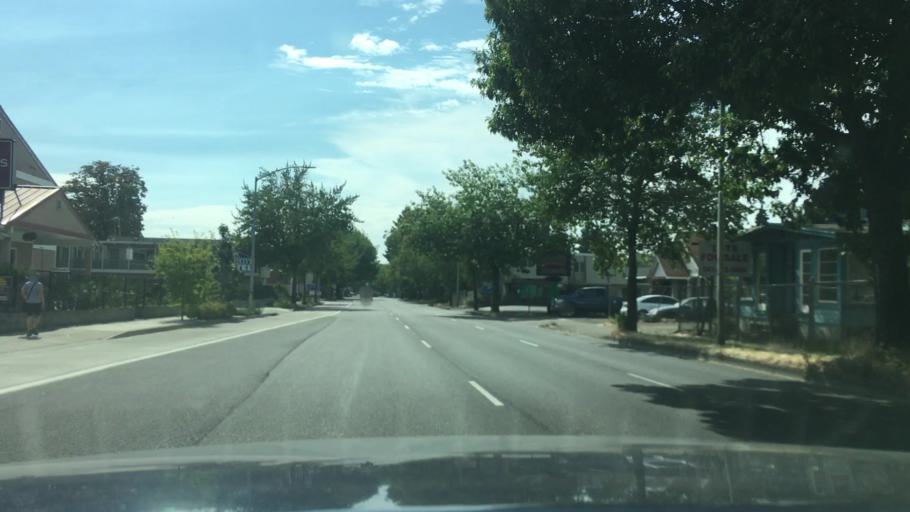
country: US
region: Oregon
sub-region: Lane County
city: Eugene
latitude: 44.0533
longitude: -123.1079
